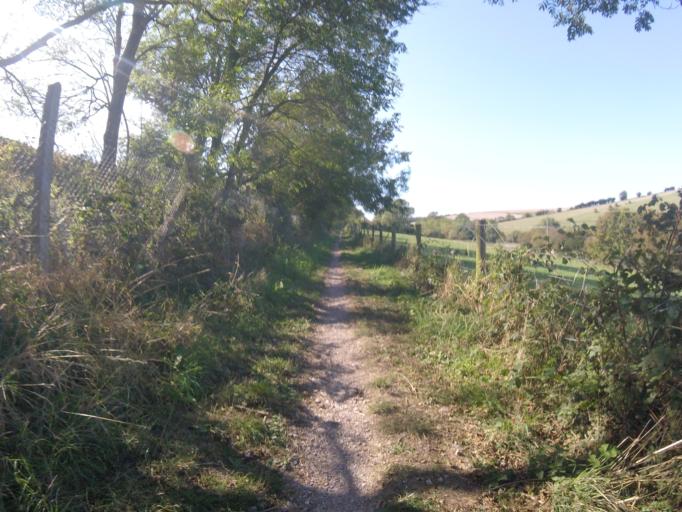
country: GB
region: England
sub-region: Brighton and Hove
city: Rottingdean
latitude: 50.8649
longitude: -0.0505
